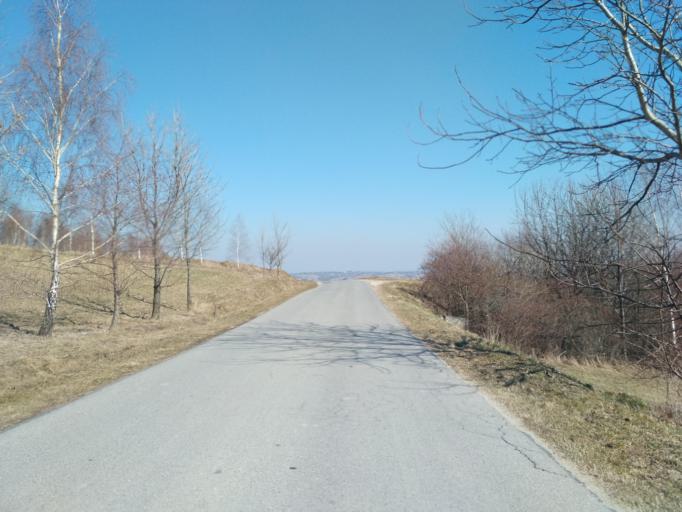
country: PL
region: Subcarpathian Voivodeship
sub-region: Powiat strzyzowski
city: Czudec
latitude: 49.9799
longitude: 21.8422
